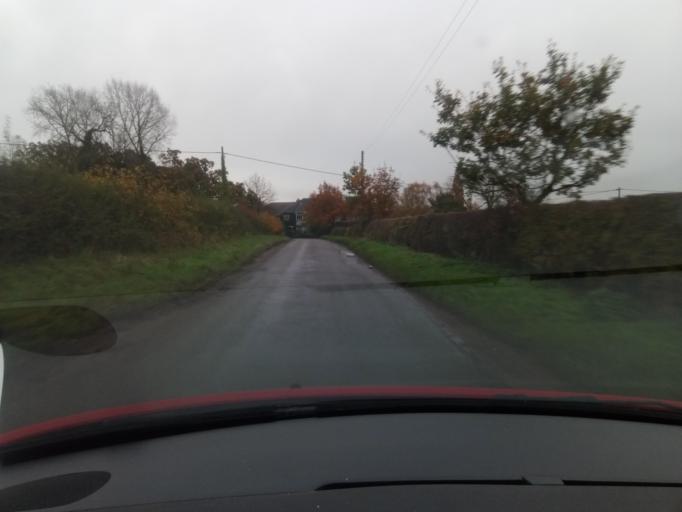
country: GB
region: England
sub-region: Derbyshire
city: Borrowash
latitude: 52.8642
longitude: -1.3987
